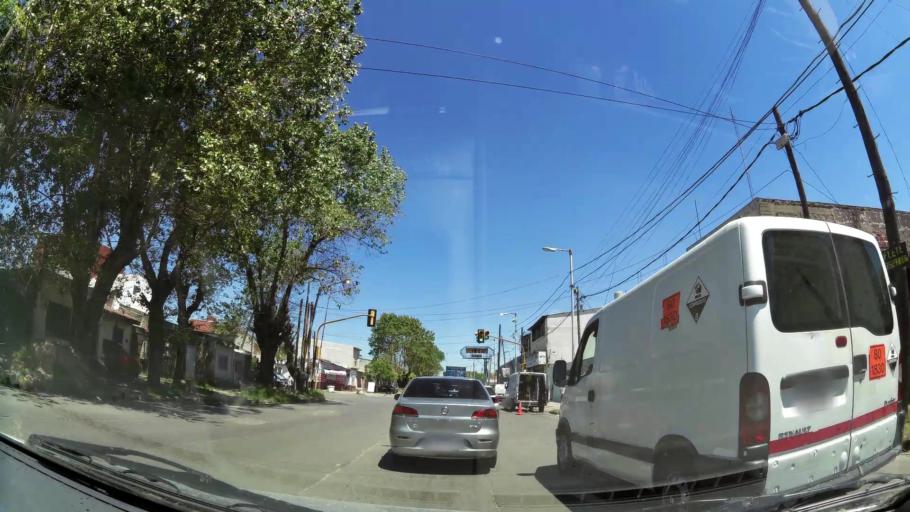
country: AR
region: Buenos Aires
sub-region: Partido de Quilmes
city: Quilmes
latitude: -34.7166
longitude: -58.3223
